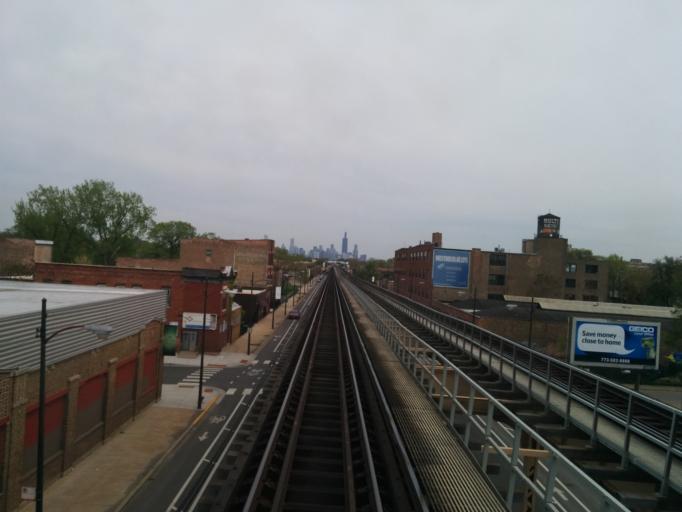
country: US
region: Illinois
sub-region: Cook County
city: Cicero
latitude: 41.8859
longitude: -87.7334
